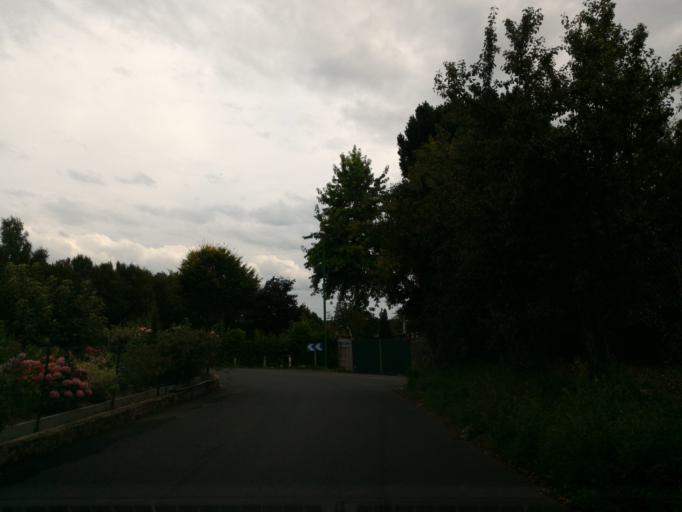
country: FR
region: Lower Normandy
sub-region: Departement de la Manche
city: La Haye-Pesnel
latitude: 48.7831
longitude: -1.4286
